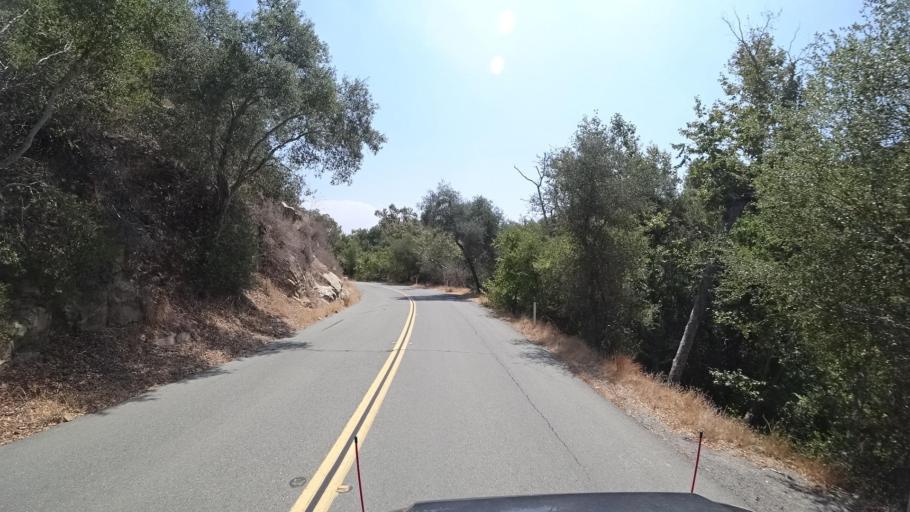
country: US
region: California
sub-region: San Diego County
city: Bonsall
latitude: 33.3157
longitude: -117.2353
